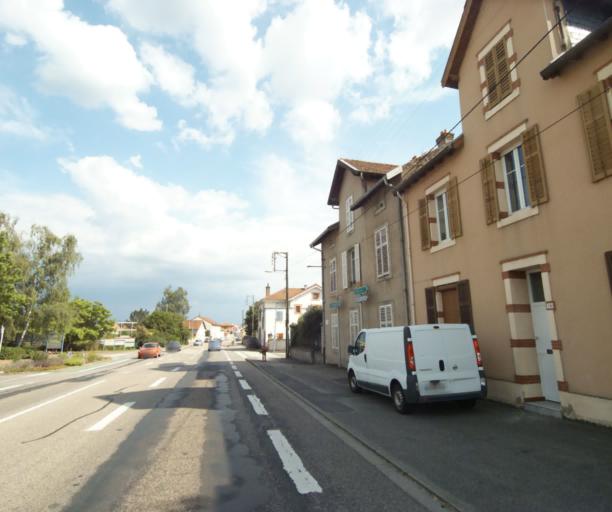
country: FR
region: Lorraine
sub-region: Departement de Meurthe-et-Moselle
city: Chanteheux
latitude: 48.5775
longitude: 6.5240
